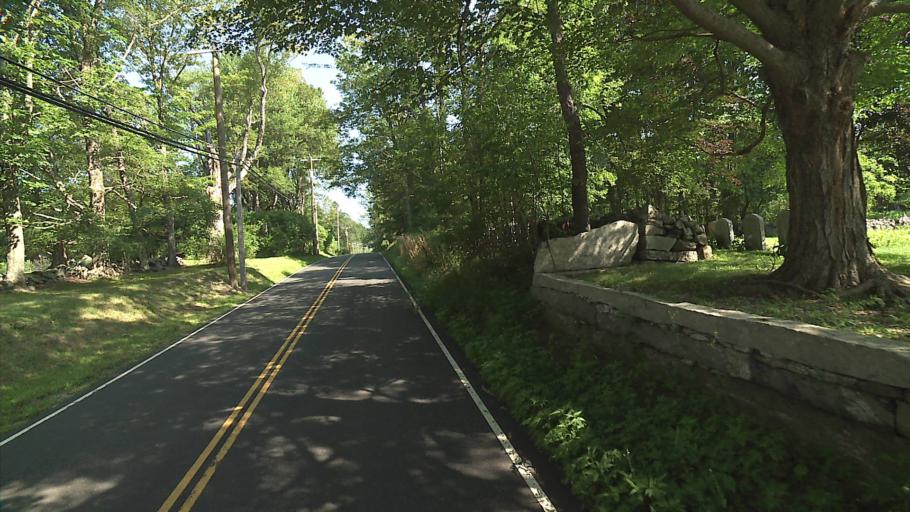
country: US
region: Connecticut
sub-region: Litchfield County
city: Winsted
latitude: 41.9928
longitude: -73.0986
